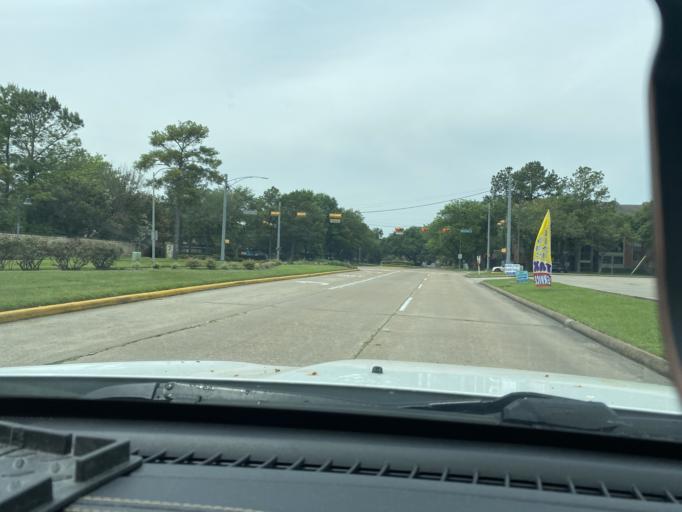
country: US
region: Texas
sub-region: Harris County
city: Jersey Village
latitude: 29.9098
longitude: -95.5794
